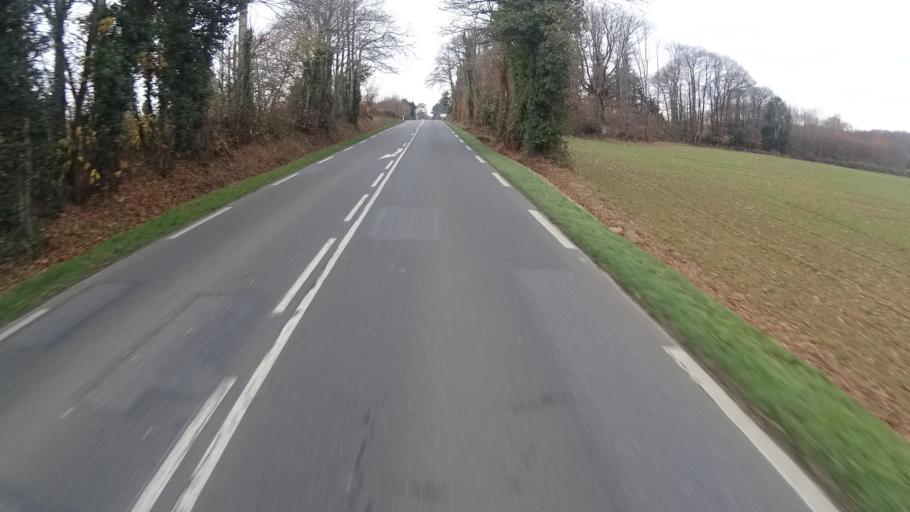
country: FR
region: Pays de la Loire
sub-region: Departement de la Loire-Atlantique
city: Avessac
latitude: 47.6411
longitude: -2.0208
